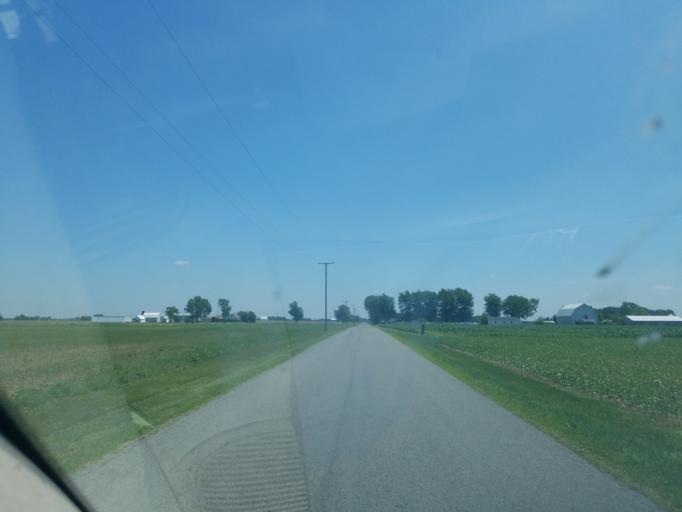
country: US
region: Ohio
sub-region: Allen County
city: Spencerville
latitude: 40.7575
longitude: -84.3740
